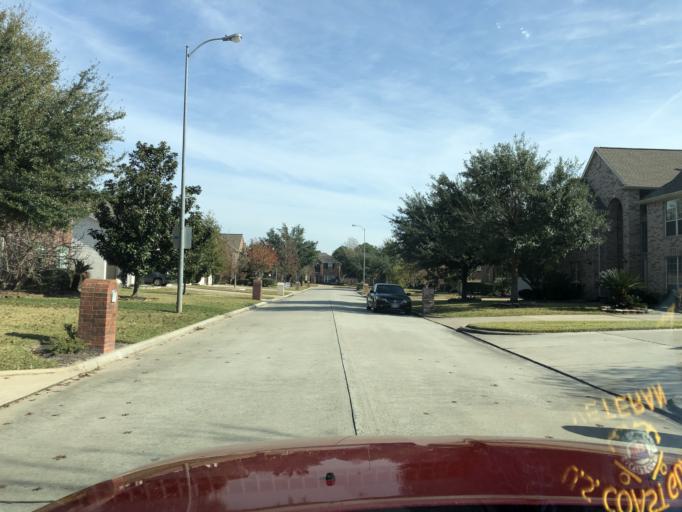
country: US
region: Texas
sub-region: Harris County
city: Tomball
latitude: 30.0269
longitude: -95.5585
